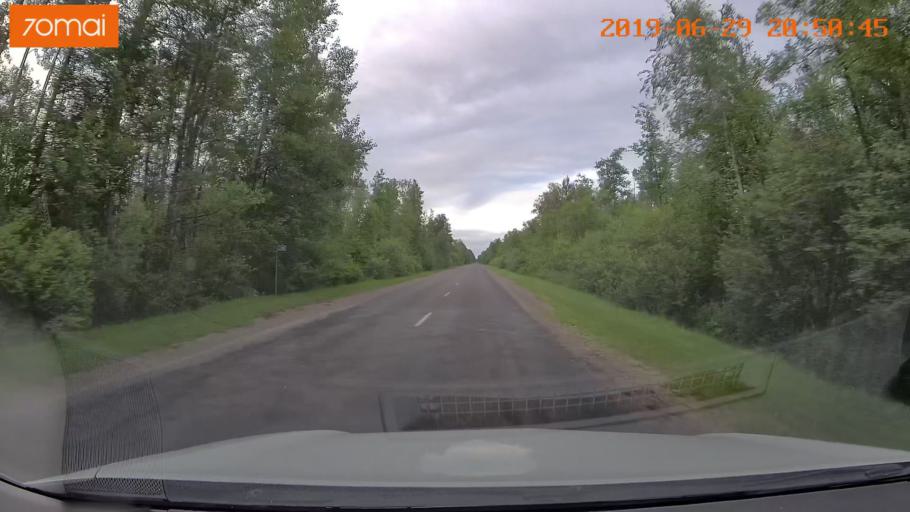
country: BY
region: Brest
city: Hantsavichy
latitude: 52.6801
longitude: 26.3401
